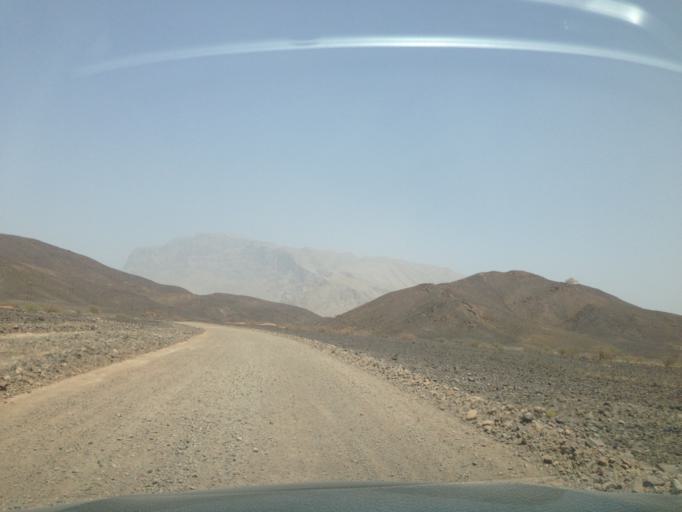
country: OM
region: Az Zahirah
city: `Ibri
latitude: 23.1996
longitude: 56.8773
